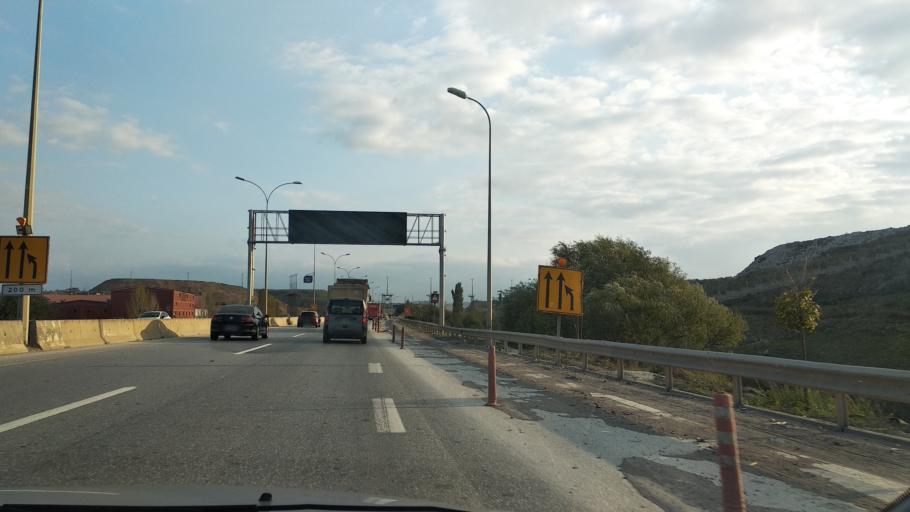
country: TR
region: Istanbul
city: Pendik
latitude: 40.9094
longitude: 29.3268
